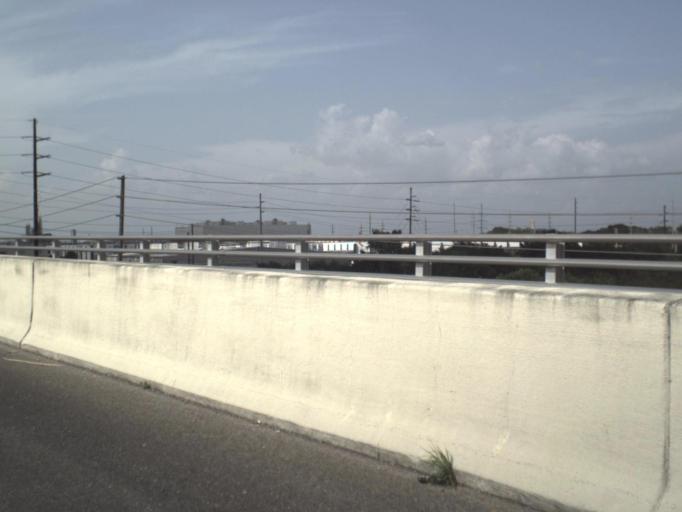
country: US
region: Florida
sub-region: Polk County
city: Lake Wales
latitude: 27.9038
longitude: -81.6004
